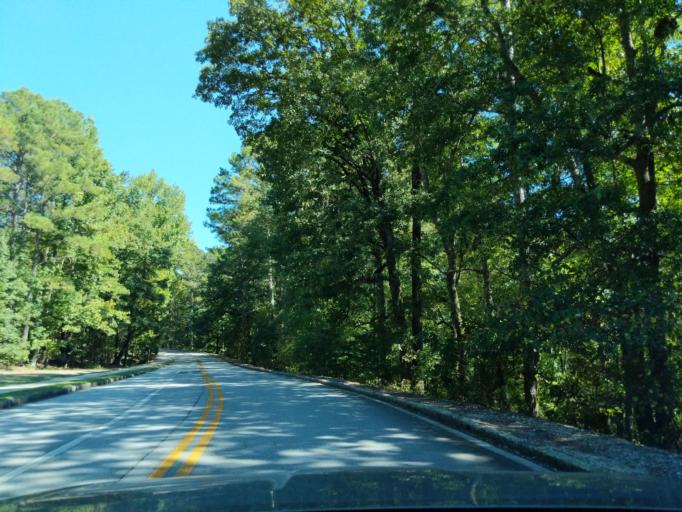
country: US
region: Georgia
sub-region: DeKalb County
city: Stone Mountain
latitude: 33.7987
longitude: -84.1413
